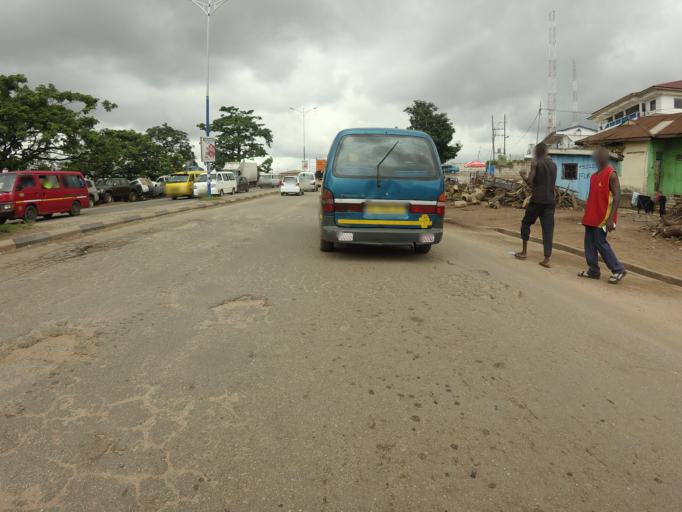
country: GH
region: Ashanti
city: Tafo
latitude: 6.7264
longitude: -1.6316
